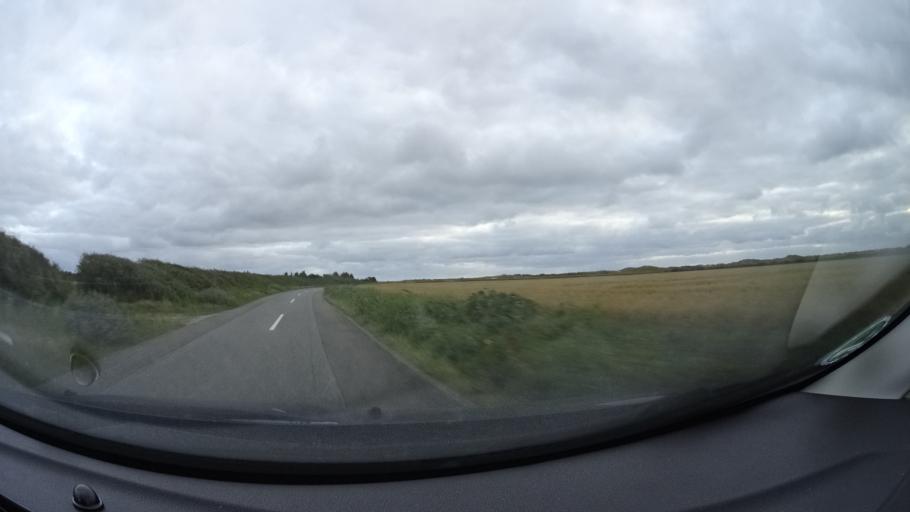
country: DK
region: Central Jutland
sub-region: Ringkobing-Skjern Kommune
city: Ringkobing
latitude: 56.1531
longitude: 8.1382
